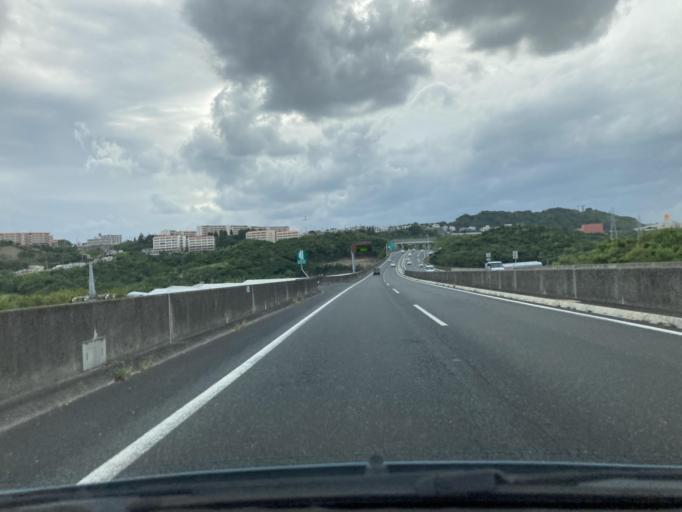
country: JP
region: Okinawa
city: Tomigusuku
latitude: 26.1740
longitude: 127.7032
